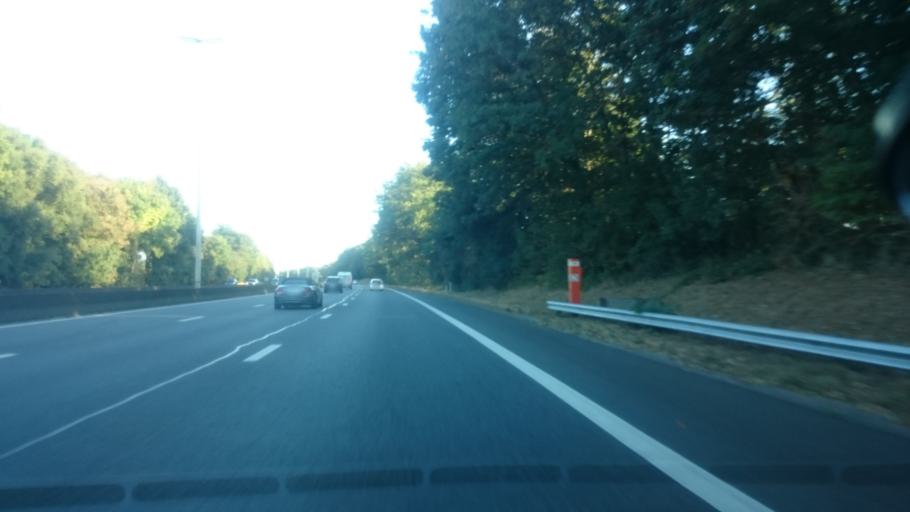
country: BE
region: Wallonia
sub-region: Province du Brabant Wallon
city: Louvain-la-Neuve
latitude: 50.6688
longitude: 4.6353
